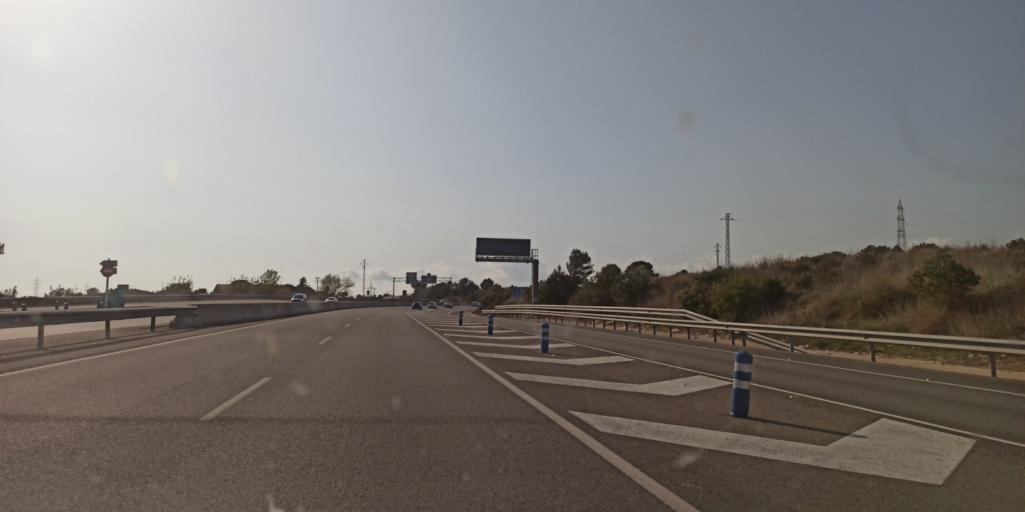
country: ES
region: Catalonia
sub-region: Provincia de Barcelona
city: Vilafranca del Penedes
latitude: 41.3223
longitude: 1.7173
